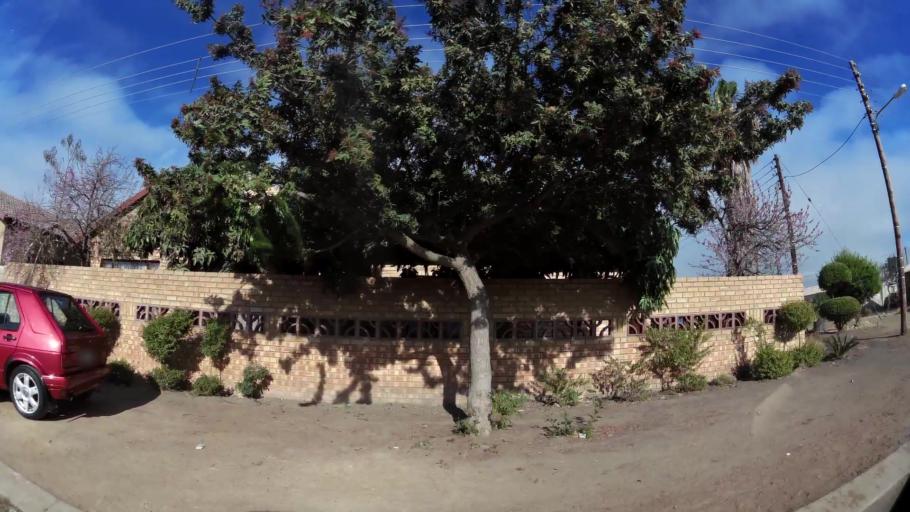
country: ZA
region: Limpopo
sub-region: Capricorn District Municipality
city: Polokwane
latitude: -23.8453
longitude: 29.3927
